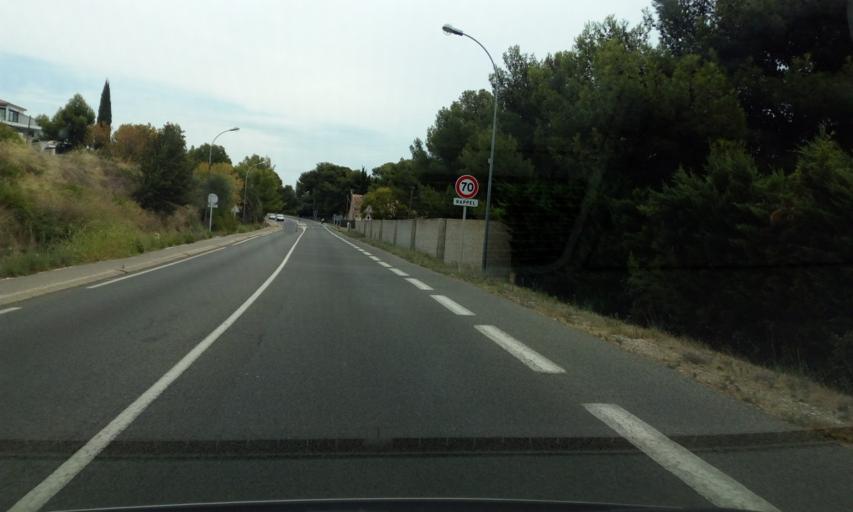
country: FR
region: Provence-Alpes-Cote d'Azur
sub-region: Departement du Var
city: Carqueiranne
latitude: 43.0862
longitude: 6.0954
